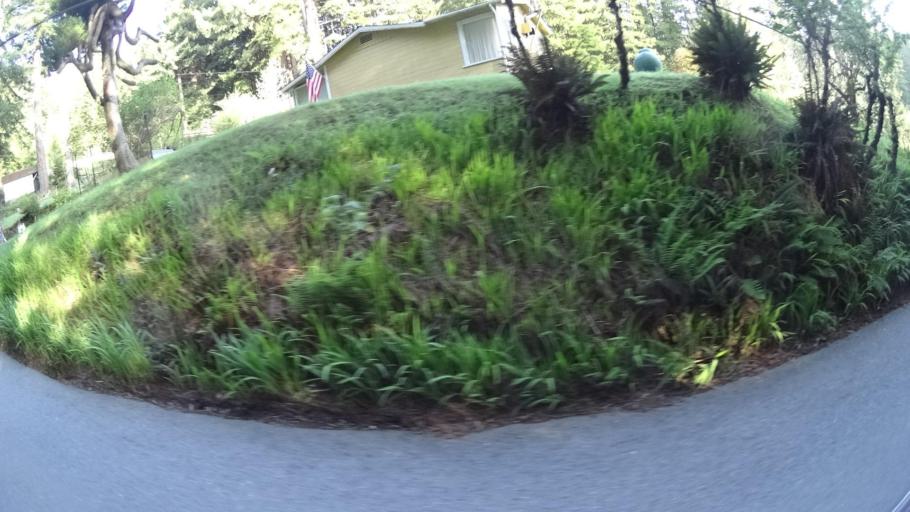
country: US
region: California
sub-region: Humboldt County
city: Myrtletown
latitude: 40.7737
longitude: -124.1133
